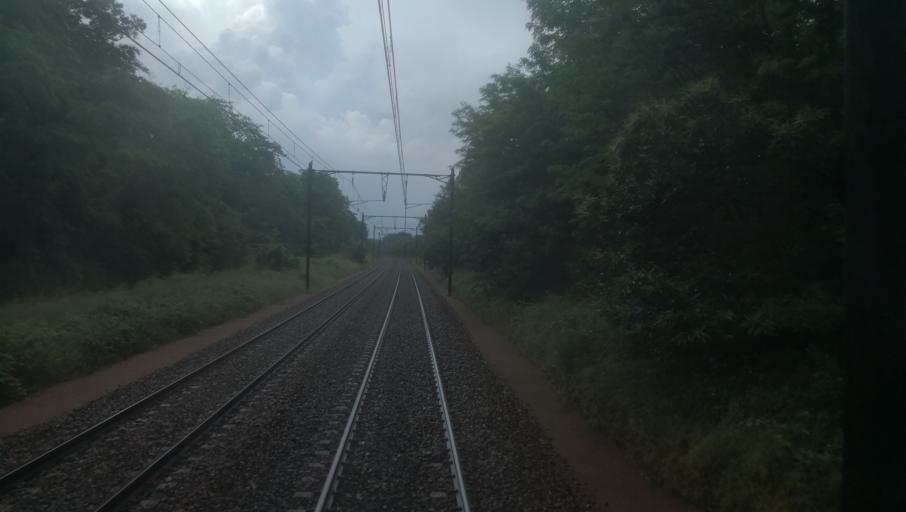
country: FR
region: Centre
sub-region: Departement du Loiret
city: Saint-Cyr-en-Val
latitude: 47.8301
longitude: 1.9489
